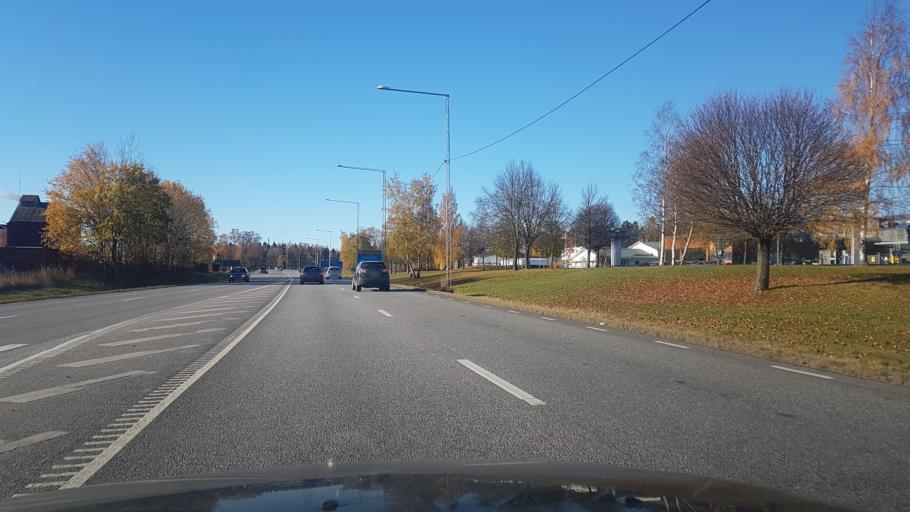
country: SE
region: Stockholm
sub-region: Sigtuna Kommun
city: Marsta
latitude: 59.6134
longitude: 17.8731
